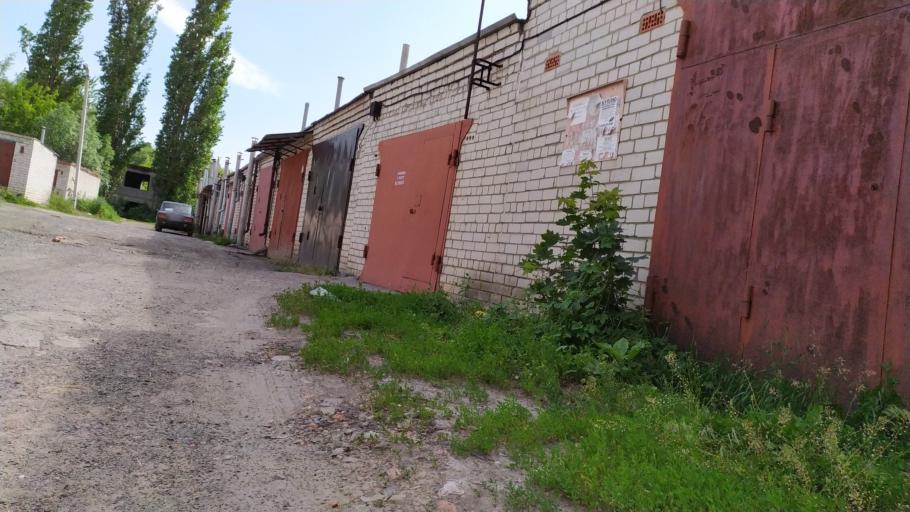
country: RU
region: Kursk
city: Kursk
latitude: 51.6636
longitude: 36.1521
